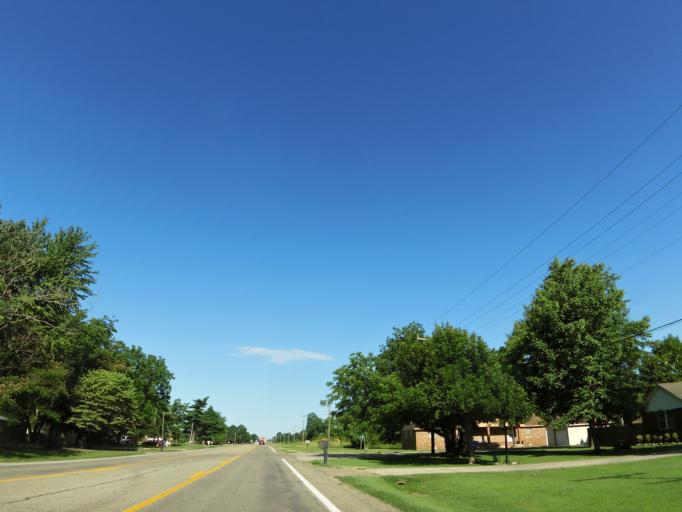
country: US
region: Arkansas
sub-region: Clay County
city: Corning
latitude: 36.4115
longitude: -90.6039
